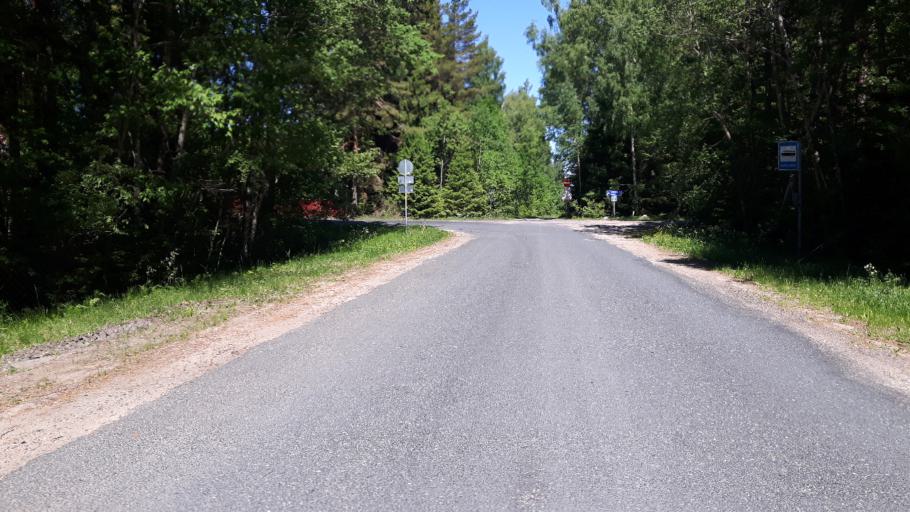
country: EE
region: Harju
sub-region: Loksa linn
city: Loksa
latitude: 59.5771
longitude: 25.6107
